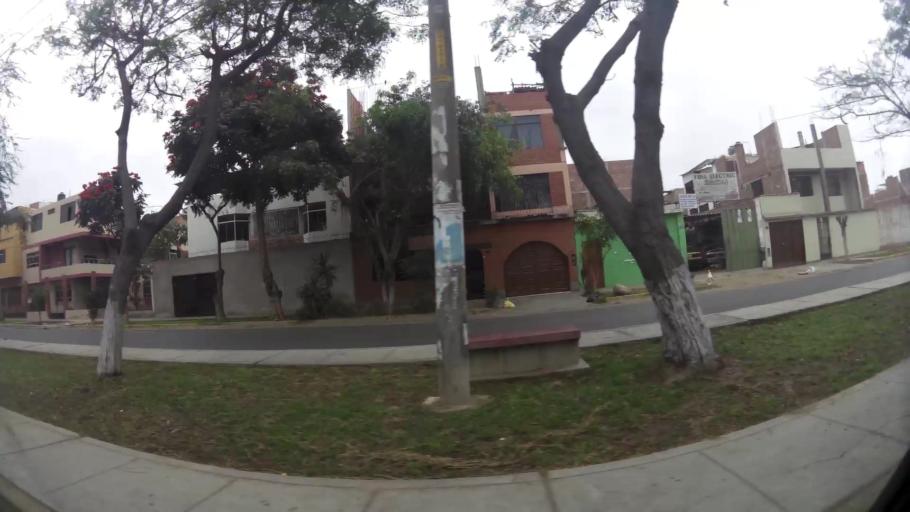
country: PE
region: La Libertad
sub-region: Provincia de Trujillo
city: Trujillo
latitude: -8.1091
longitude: -79.0375
